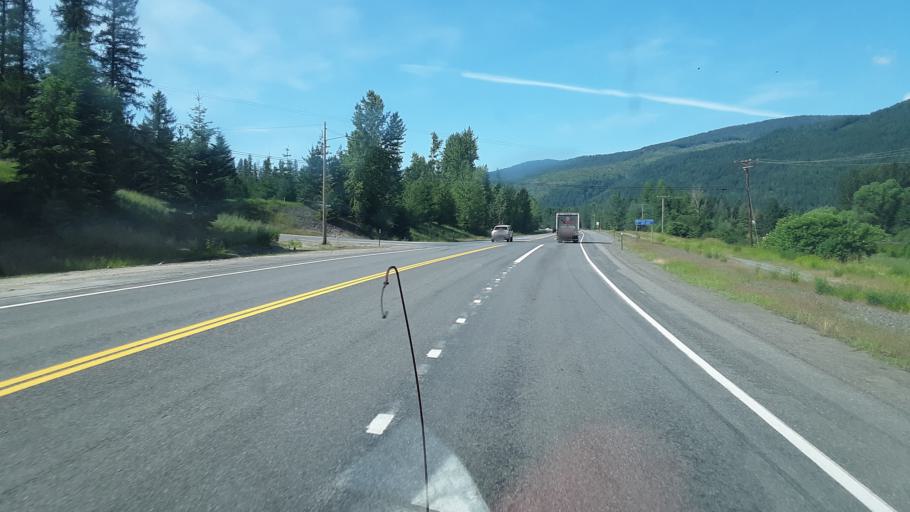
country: US
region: Idaho
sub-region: Bonner County
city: Ponderay
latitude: 48.4013
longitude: -116.5302
